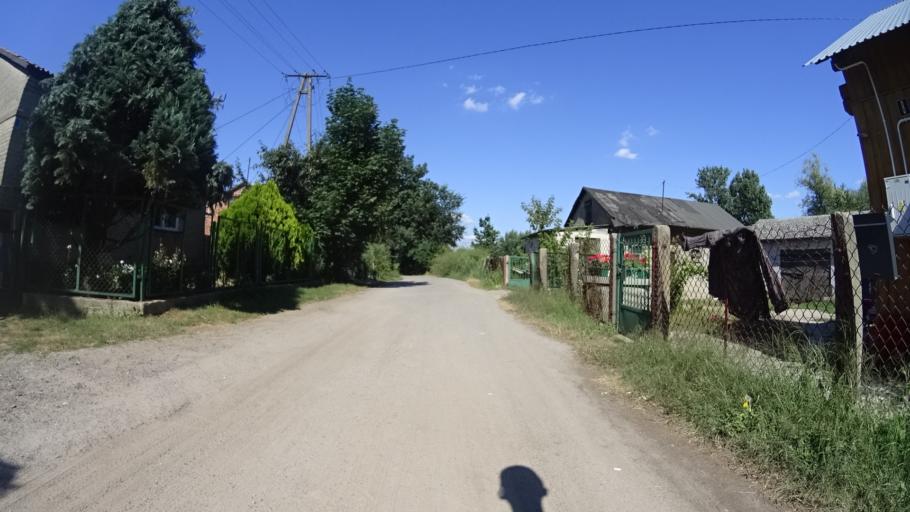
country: PL
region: Masovian Voivodeship
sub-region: Powiat bialobrzeski
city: Wysmierzyce
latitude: 51.6568
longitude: 20.8277
